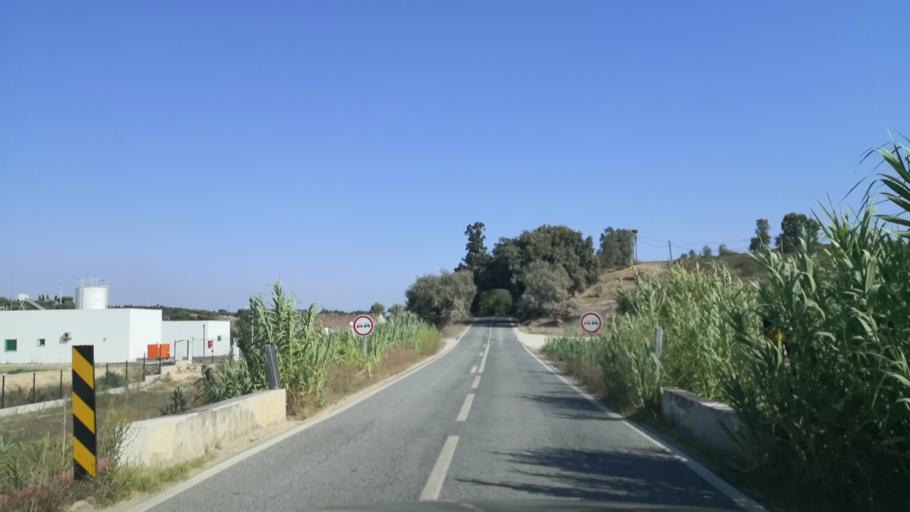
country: PT
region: Santarem
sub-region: Benavente
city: Poceirao
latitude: 38.7677
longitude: -8.6223
